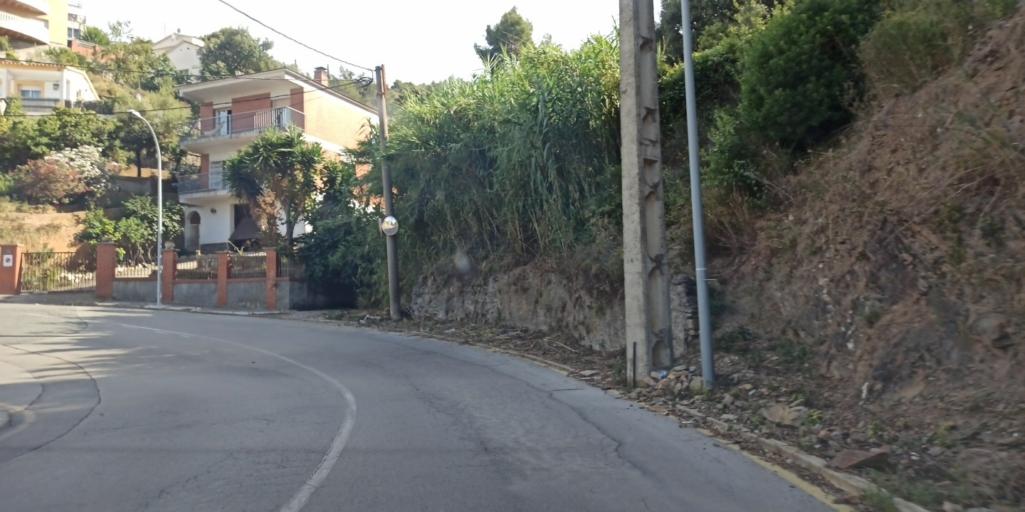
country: ES
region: Catalonia
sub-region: Provincia de Barcelona
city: Santa Coloma de Cervello
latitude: 41.3598
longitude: 2.0013
